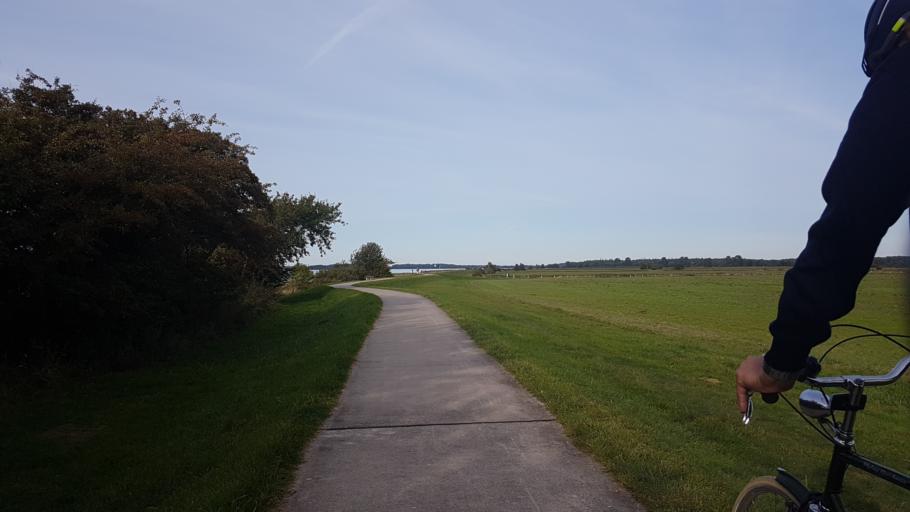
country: DE
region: Mecklenburg-Vorpommern
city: Hiddensee
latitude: 54.4749
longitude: 13.1426
